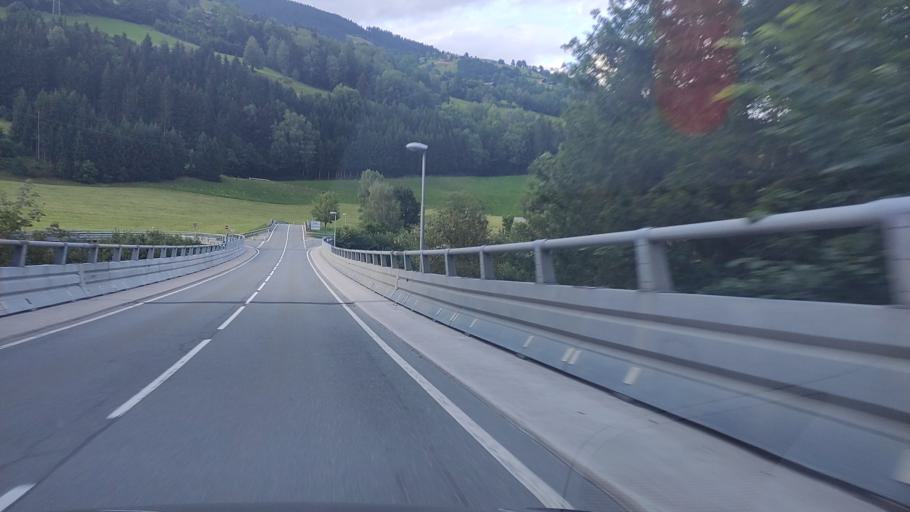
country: AT
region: Salzburg
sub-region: Politischer Bezirk Zell am See
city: Taxenbach
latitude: 47.2913
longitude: 12.9545
